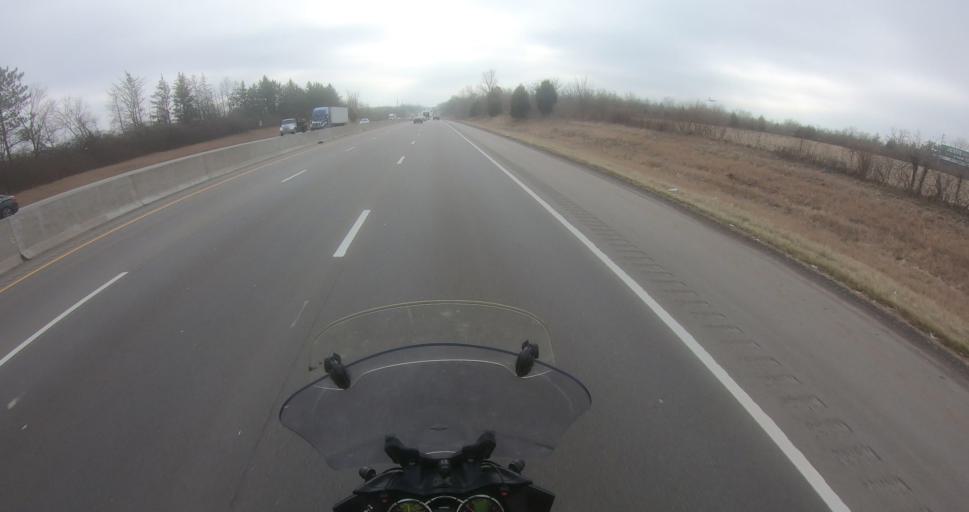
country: US
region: Ohio
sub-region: Miami County
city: Tipp City
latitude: 39.9356
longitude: -84.1895
